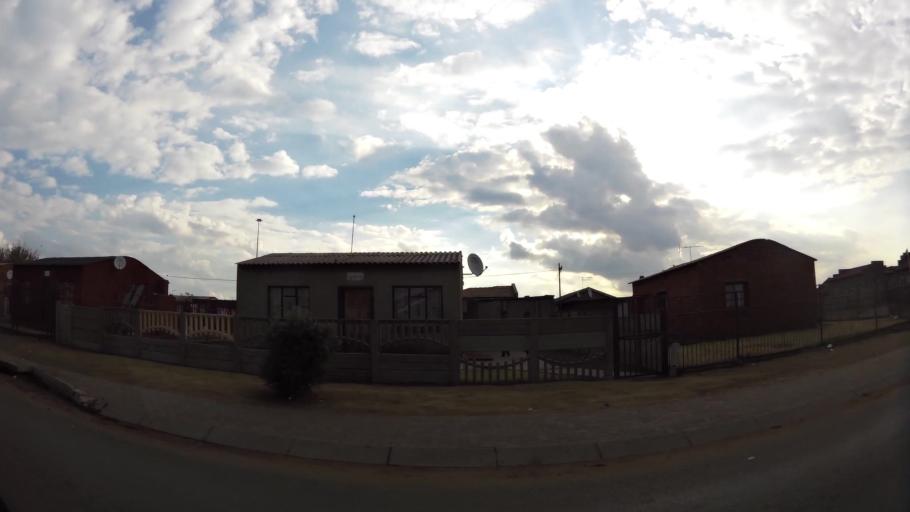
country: ZA
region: Gauteng
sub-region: Sedibeng District Municipality
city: Vanderbijlpark
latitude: -26.6935
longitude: 27.8748
